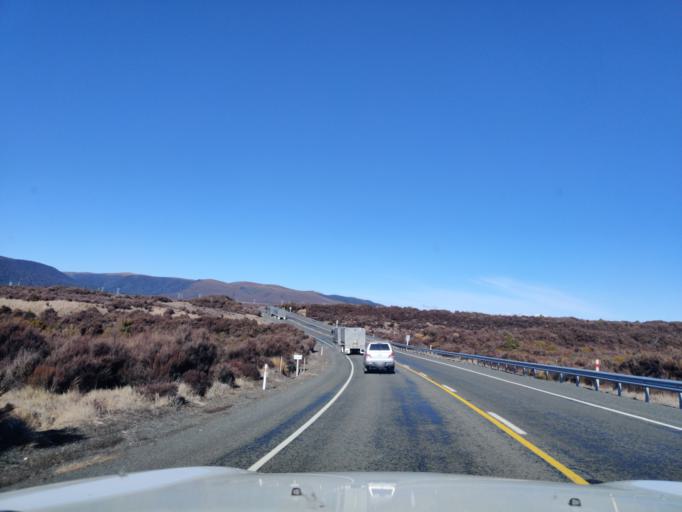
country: NZ
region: Manawatu-Wanganui
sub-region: Ruapehu District
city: Waiouru
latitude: -39.2409
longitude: 175.7265
